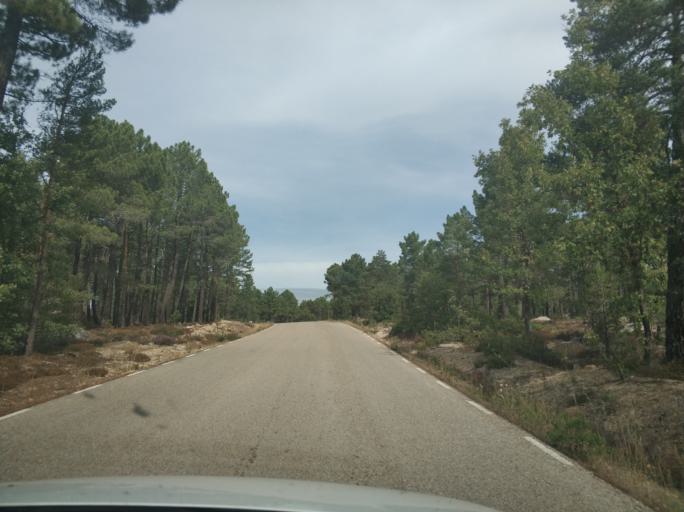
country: ES
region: Castille and Leon
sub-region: Provincia de Soria
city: Duruelo de la Sierra
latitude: 41.8820
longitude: -2.9365
